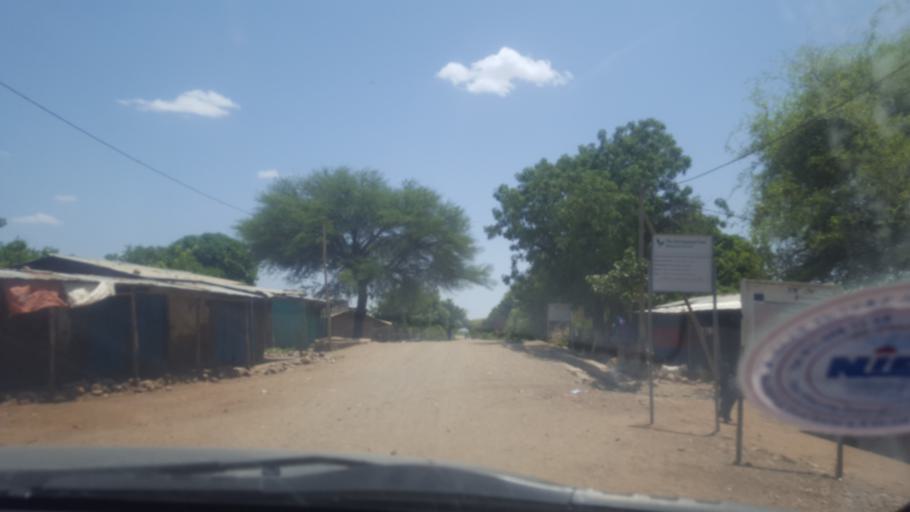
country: ET
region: Oromiya
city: Deder
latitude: 9.5309
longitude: 41.4140
